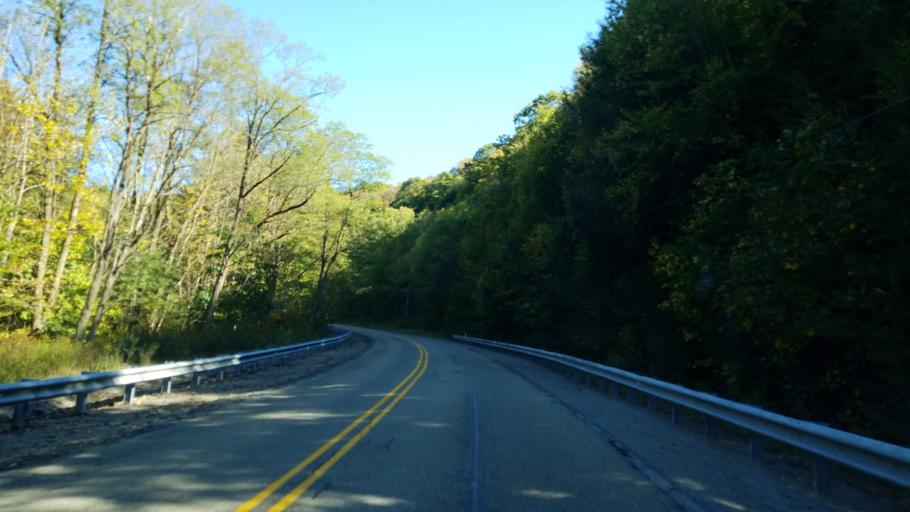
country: US
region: Pennsylvania
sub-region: Clearfield County
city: Shiloh
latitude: 41.2506
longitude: -78.3786
